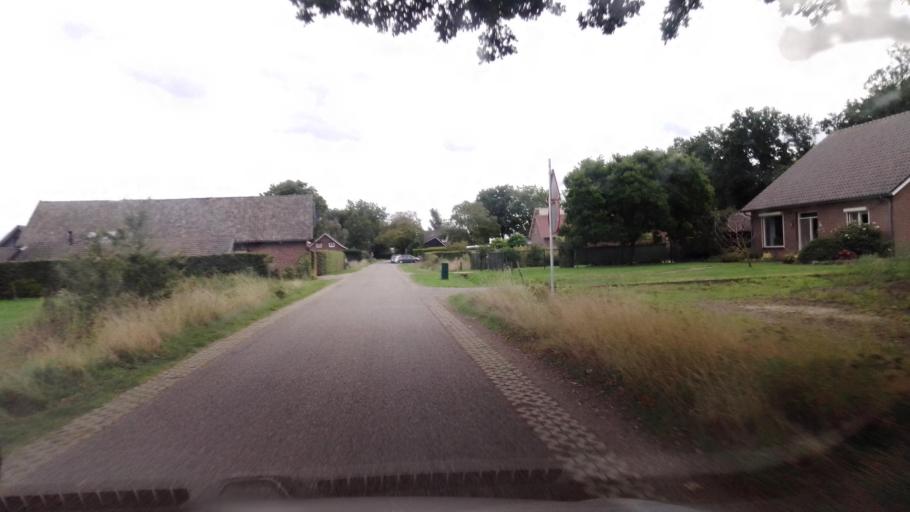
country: NL
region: Limburg
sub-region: Gemeente Peel en Maas
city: Maasbree
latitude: 51.4180
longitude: 6.0544
